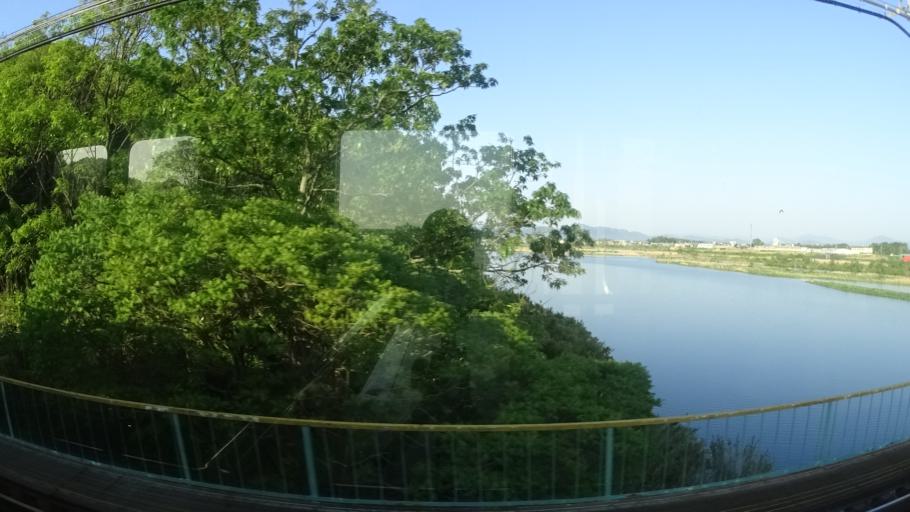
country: JP
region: Mie
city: Ise
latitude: 34.5088
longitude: 136.6902
